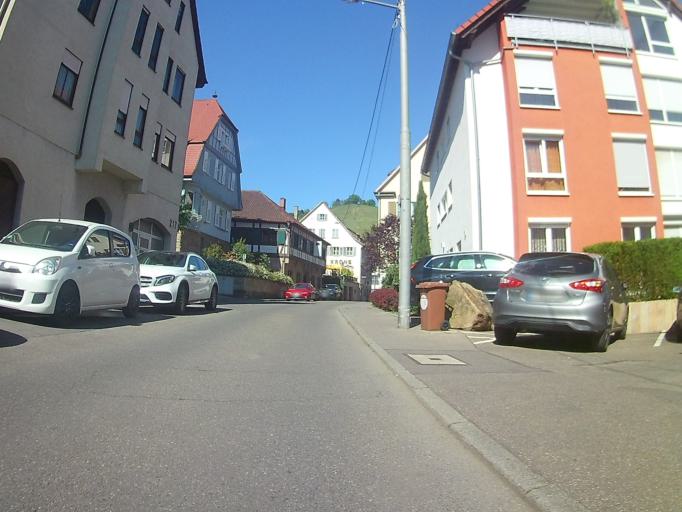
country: DE
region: Baden-Wuerttemberg
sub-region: Regierungsbezirk Stuttgart
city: Fellbach
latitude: 48.7755
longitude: 9.2775
